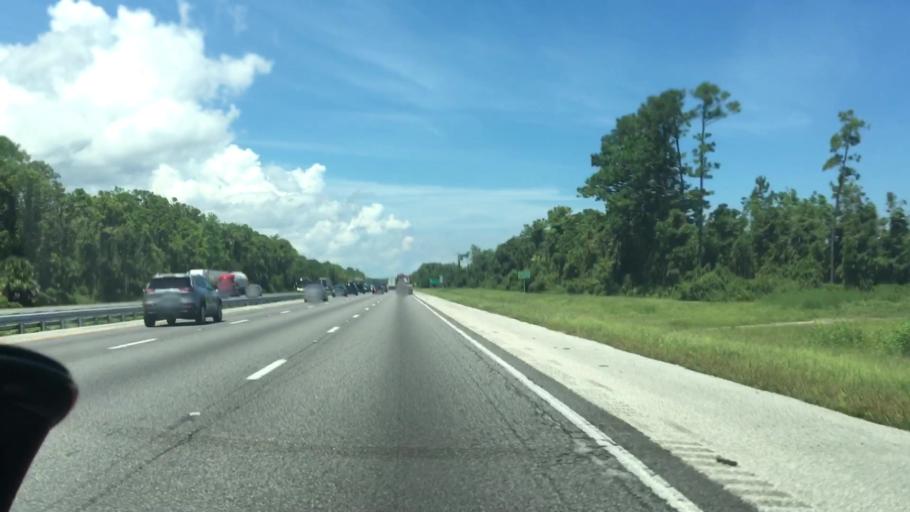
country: US
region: Florida
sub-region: Flagler County
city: Flagler Beach
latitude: 29.4138
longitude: -81.1598
